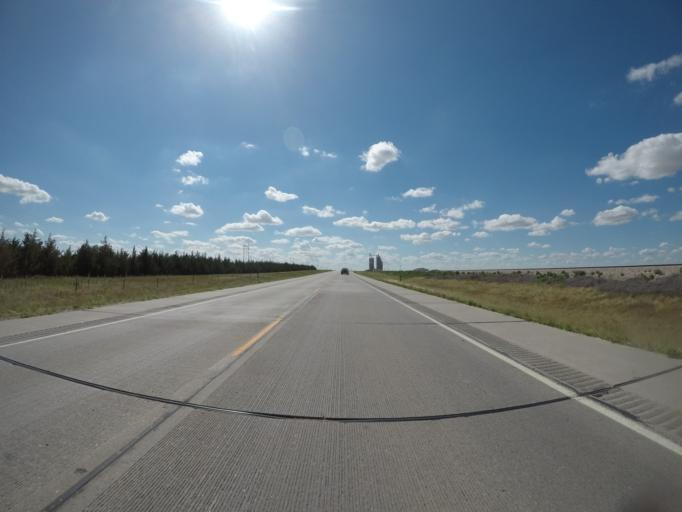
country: US
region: Colorado
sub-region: Phillips County
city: Holyoke
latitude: 40.5895
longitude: -102.3361
